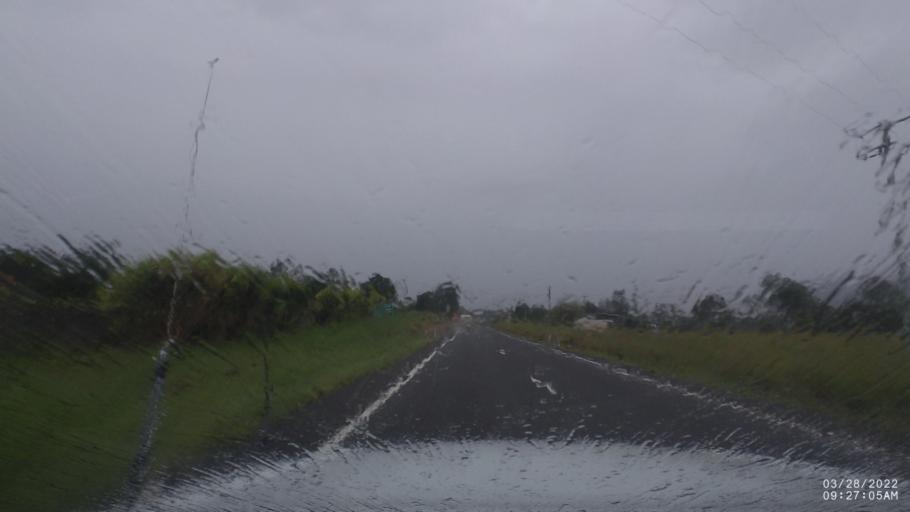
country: AU
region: Queensland
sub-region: Logan
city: Cedar Vale
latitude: -27.9062
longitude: 153.1058
